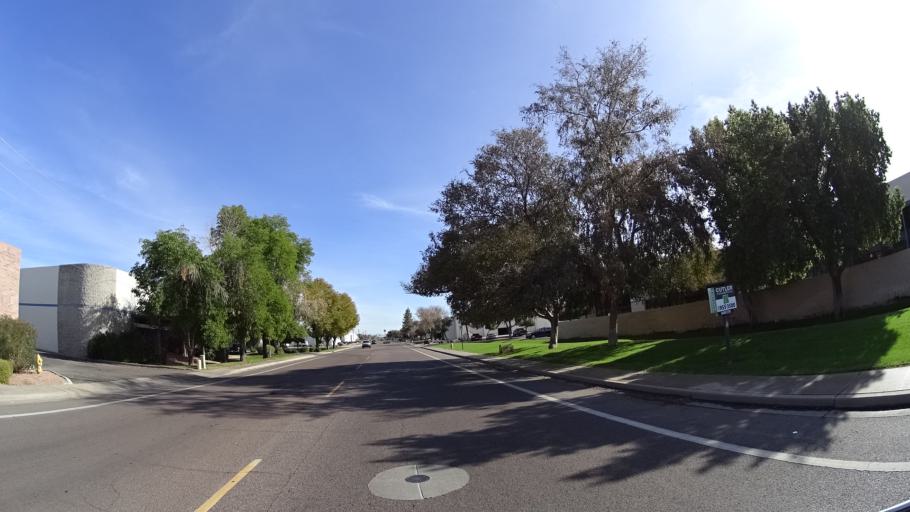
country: US
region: Arizona
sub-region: Maricopa County
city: Guadalupe
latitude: 33.3997
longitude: -112.0005
